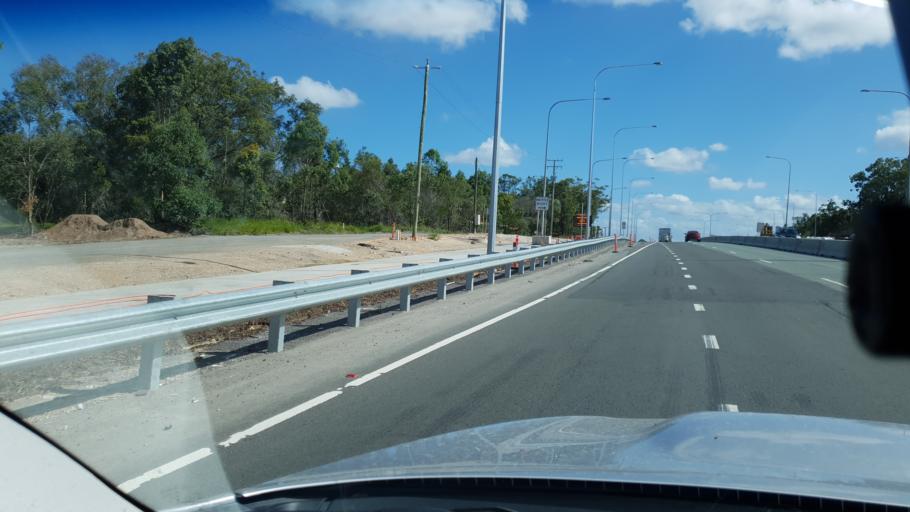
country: AU
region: Queensland
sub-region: Brisbane
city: Sunnybank Hills
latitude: -27.6497
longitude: 153.0411
